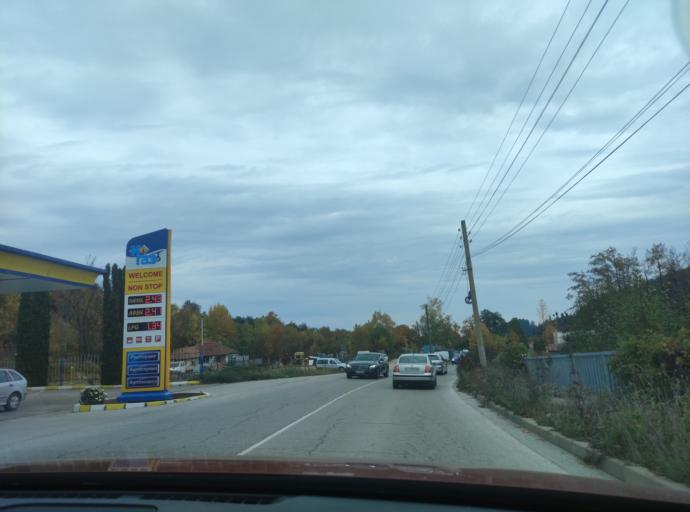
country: BG
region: Montana
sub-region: Obshtina Berkovitsa
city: Berkovitsa
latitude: 43.1881
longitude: 23.1579
